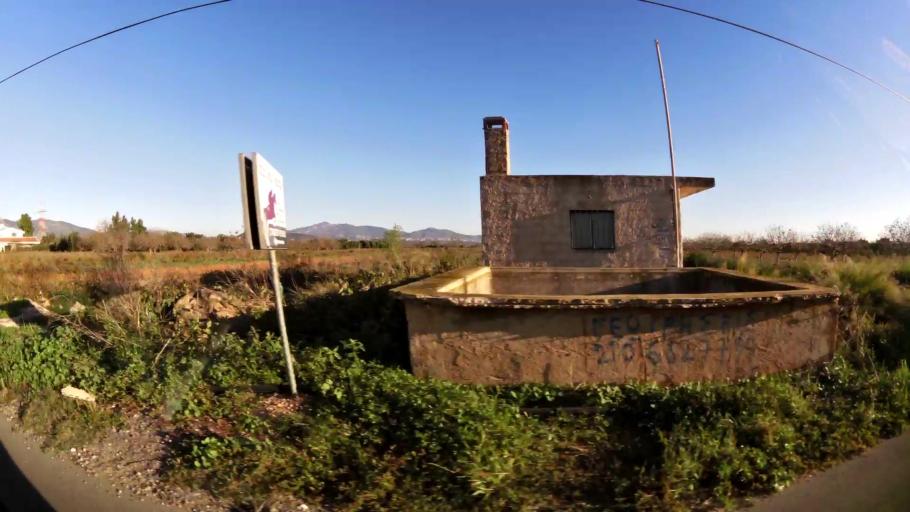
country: GR
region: Attica
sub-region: Nomarchia Anatolikis Attikis
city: Markopoulo
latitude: 37.9146
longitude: 23.9095
